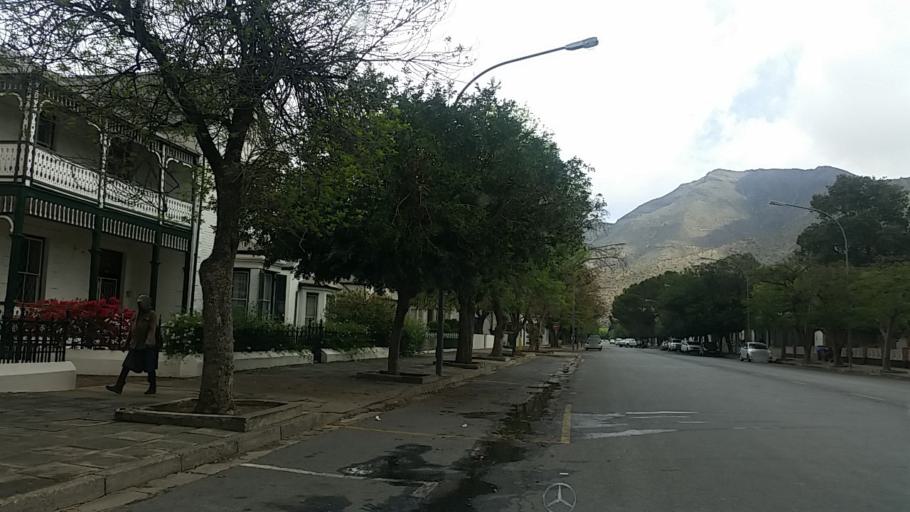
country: ZA
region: Eastern Cape
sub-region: Cacadu District Municipality
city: Graaff-Reinet
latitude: -32.2497
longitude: 24.5326
